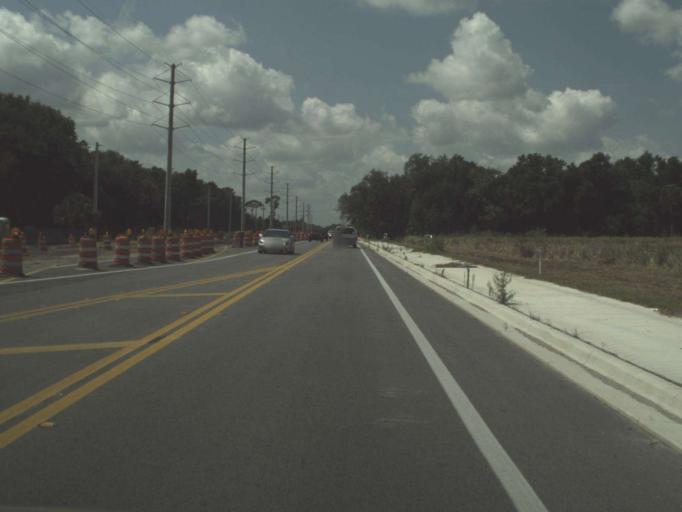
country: US
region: Florida
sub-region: Seminole County
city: Midway
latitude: 28.7960
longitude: -81.2129
